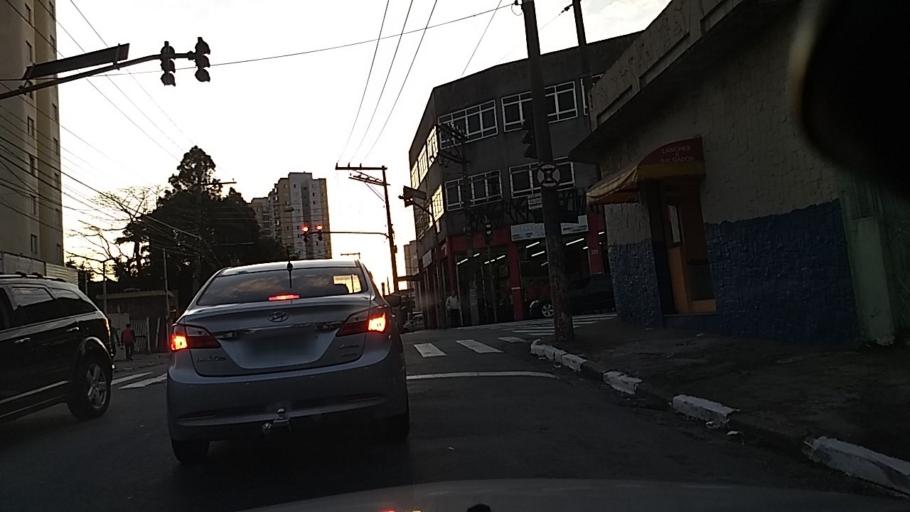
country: BR
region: Sao Paulo
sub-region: Sao Paulo
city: Sao Paulo
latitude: -23.5005
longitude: -46.5920
